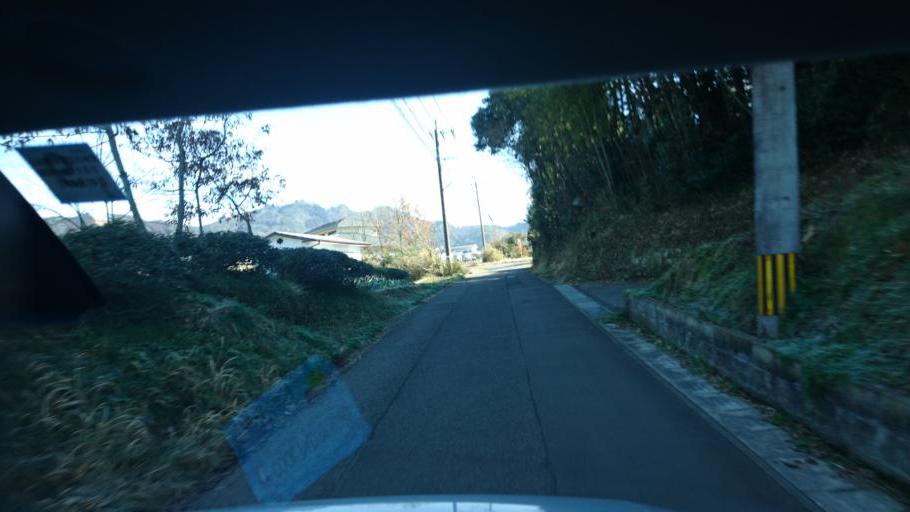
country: JP
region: Oita
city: Takedamachi
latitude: 32.6863
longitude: 131.3499
